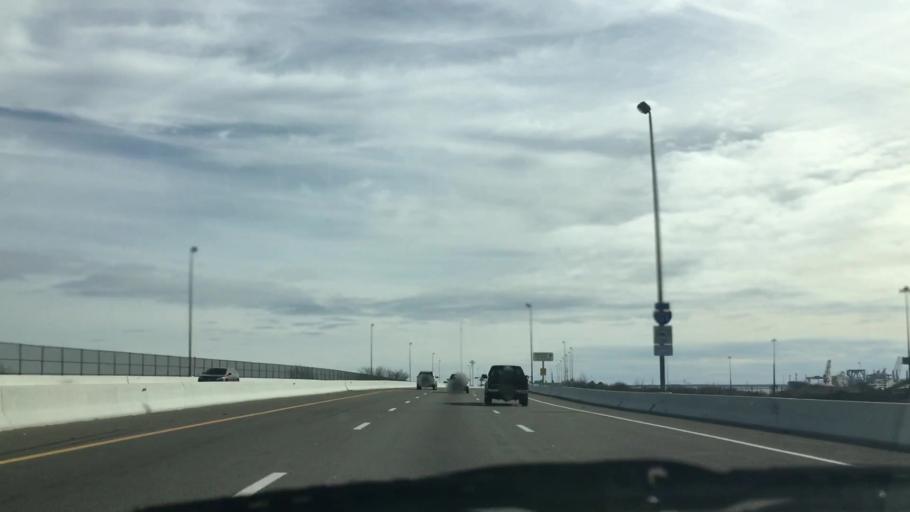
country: US
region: Virginia
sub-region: City of Newport News
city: Newport News
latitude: 36.9747
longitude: -76.4208
